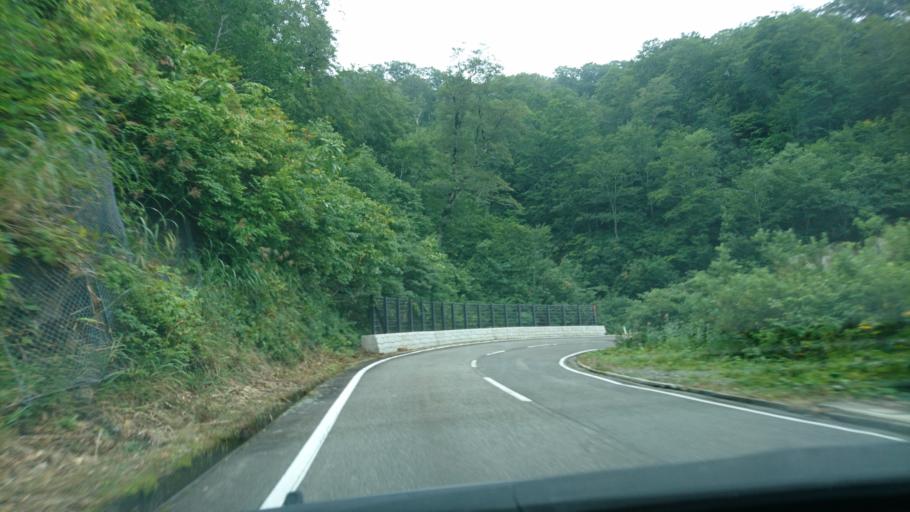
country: JP
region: Akita
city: Yuzawa
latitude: 38.9798
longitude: 140.7444
